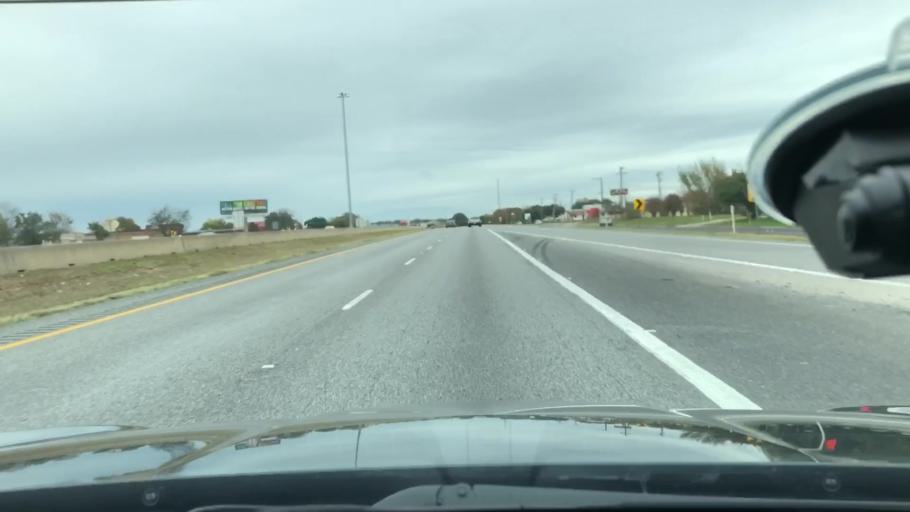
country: US
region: Texas
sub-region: Hunt County
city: Greenville
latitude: 33.1347
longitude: -96.0648
